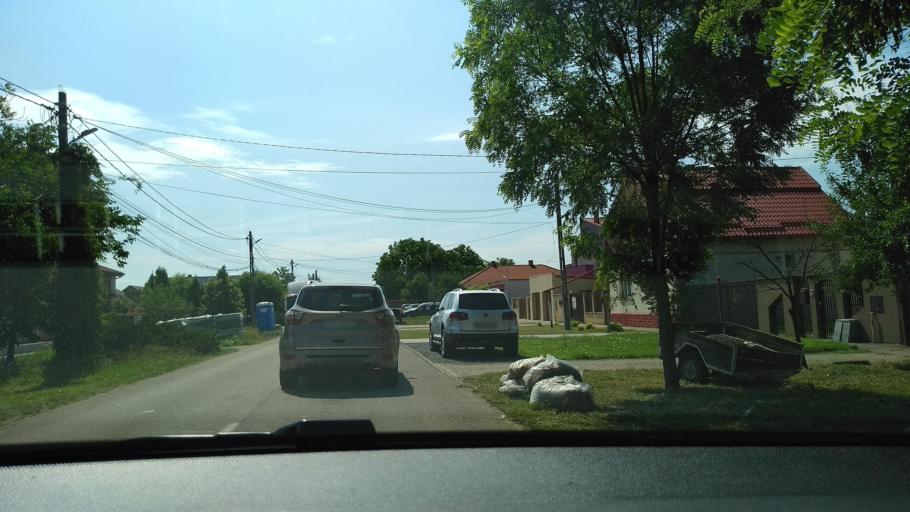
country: RO
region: Timis
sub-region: Comuna Dumbravita
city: Dumbravita
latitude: 45.8002
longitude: 21.2409
